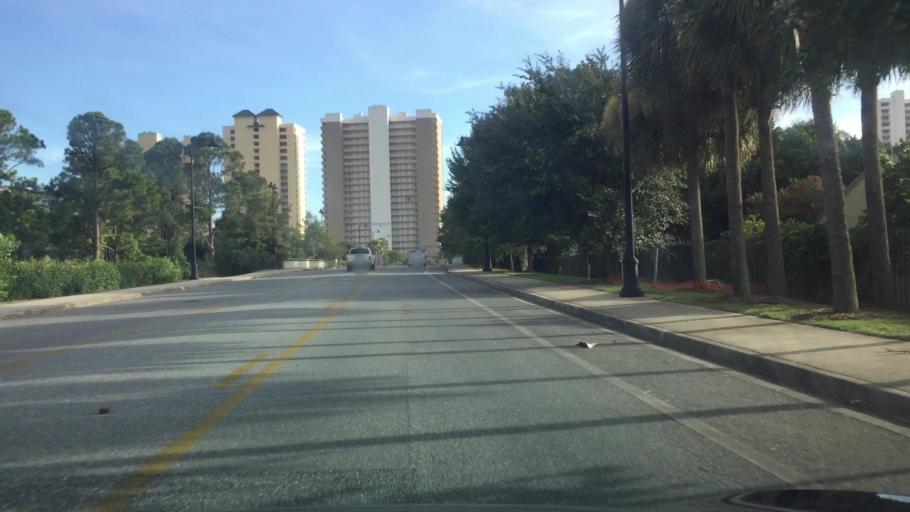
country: US
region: Florida
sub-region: Bay County
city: Panama City Beach
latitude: 30.1825
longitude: -85.8095
